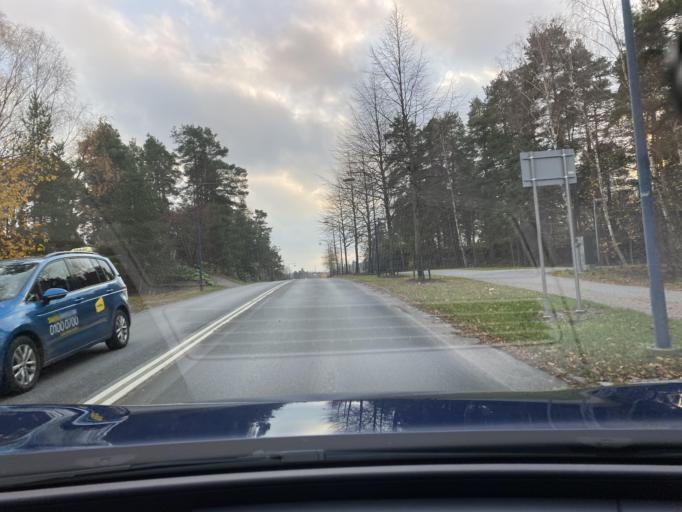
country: FI
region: Varsinais-Suomi
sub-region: Turku
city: Naantali
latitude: 60.4768
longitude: 22.0414
